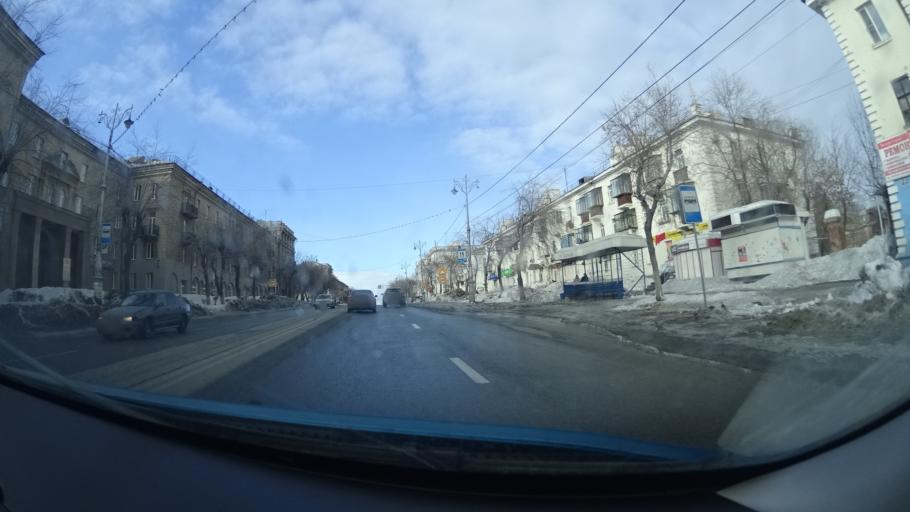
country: RU
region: Chelyabinsk
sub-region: Gorod Magnitogorsk
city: Magnitogorsk
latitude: 53.4287
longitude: 58.9836
